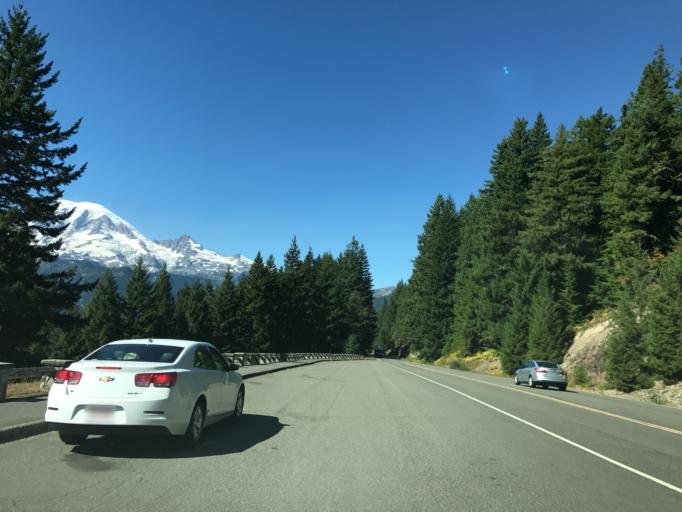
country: US
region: Washington
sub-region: Pierce County
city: Buckley
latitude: 46.7104
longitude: -121.6006
